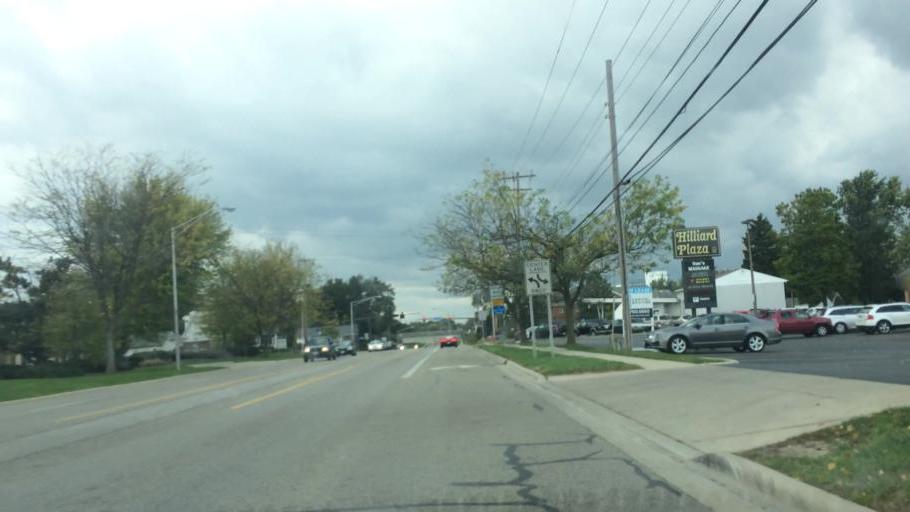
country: US
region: Ohio
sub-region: Franklin County
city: Hilliard
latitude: 40.0307
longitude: -83.1512
